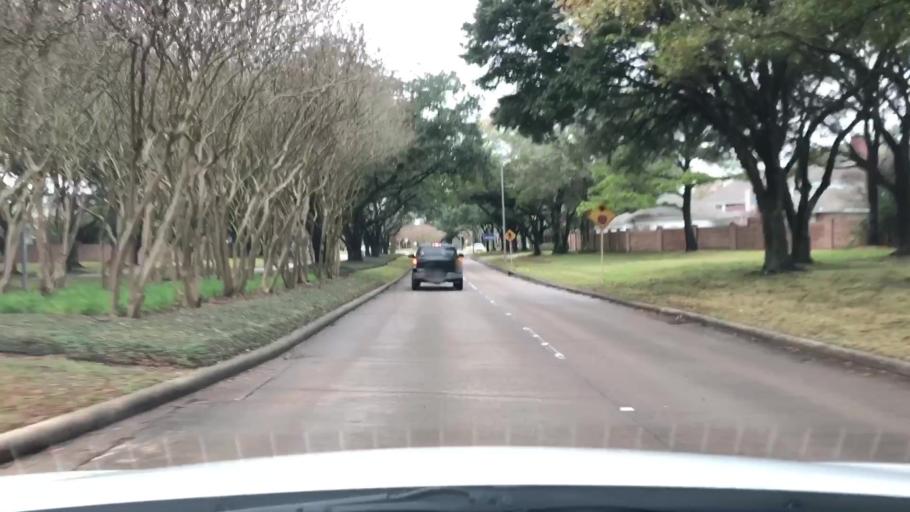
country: US
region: Texas
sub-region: Fort Bend County
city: Cinco Ranch
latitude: 29.7412
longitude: -95.7561
